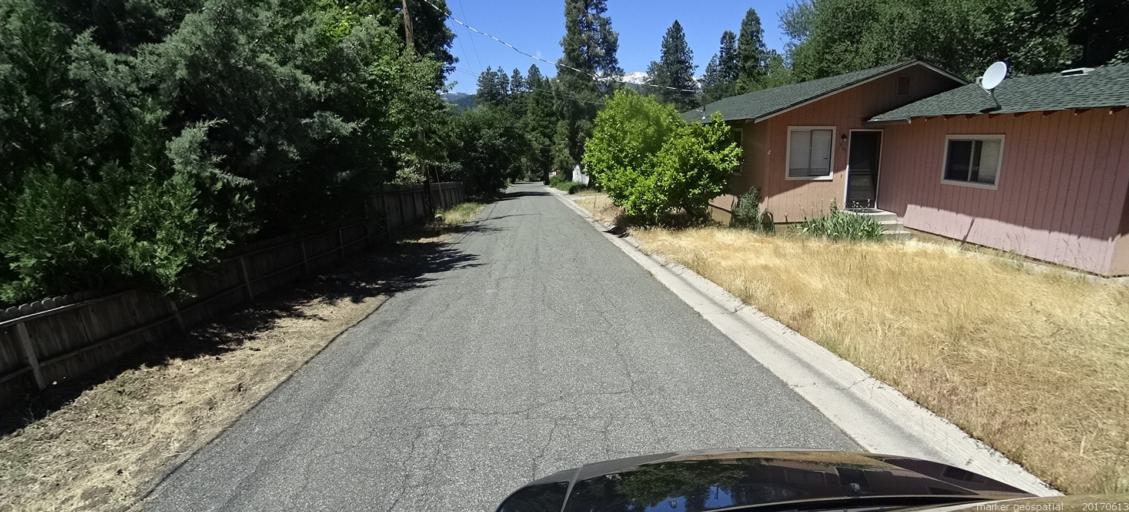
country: US
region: California
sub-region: Siskiyou County
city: Mount Shasta
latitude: 41.3089
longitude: -122.3124
